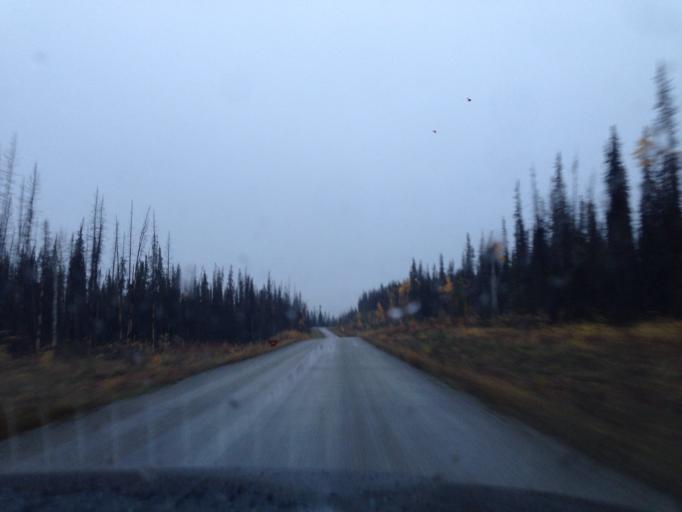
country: CA
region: Yukon
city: Watson Lake
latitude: 59.6753
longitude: -129.1603
